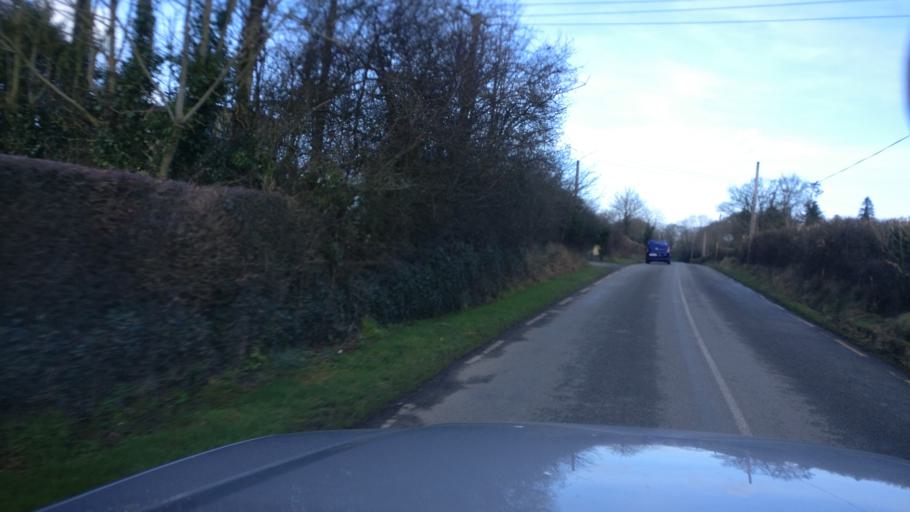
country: IE
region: Leinster
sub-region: Kilkenny
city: Castlecomer
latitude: 52.8377
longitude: -7.1922
